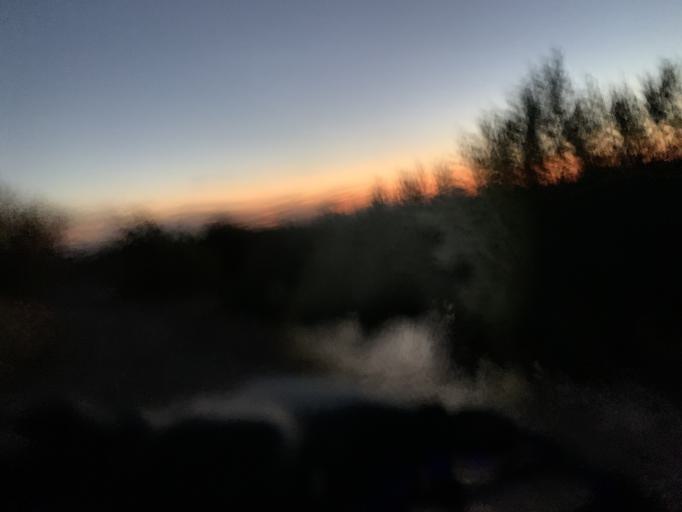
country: ES
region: Andalusia
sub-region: Provincia de Granada
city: Beas de Granada
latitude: 37.2174
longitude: -3.4688
